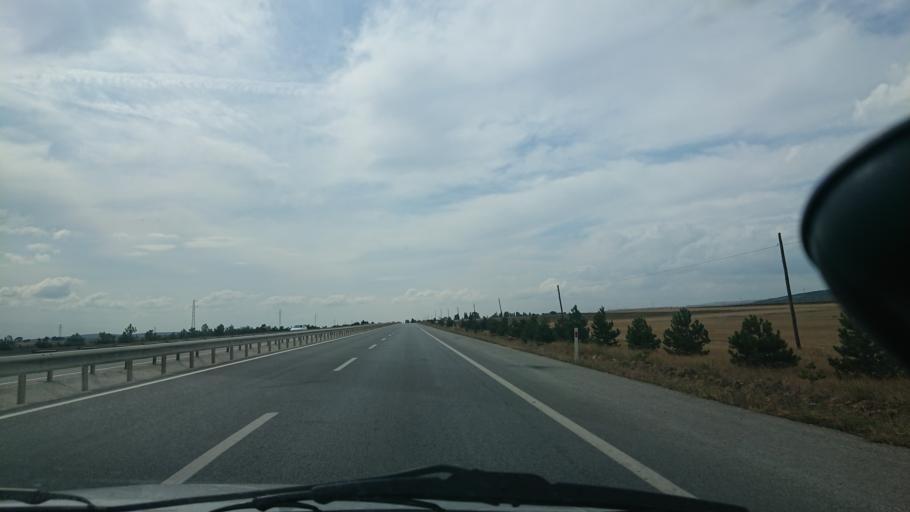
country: TR
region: Eskisehir
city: Inonu
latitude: 39.7251
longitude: 30.2848
